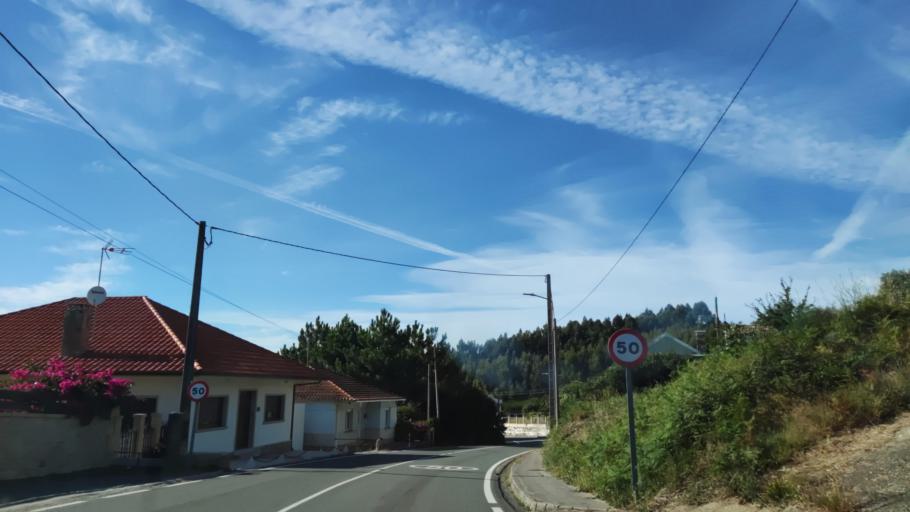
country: ES
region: Galicia
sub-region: Provincia da Coruna
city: Boiro
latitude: 42.5727
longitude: -9.0012
